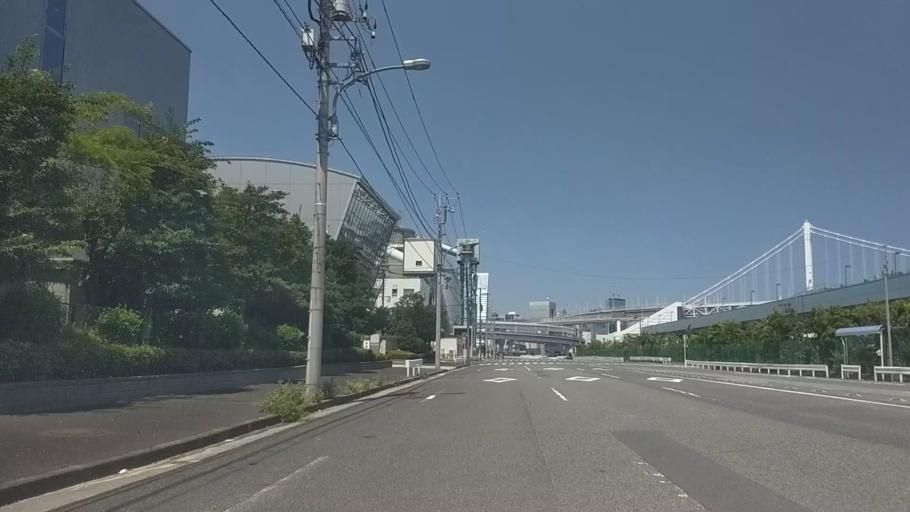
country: JP
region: Tokyo
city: Tokyo
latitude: 35.6312
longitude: 139.7574
